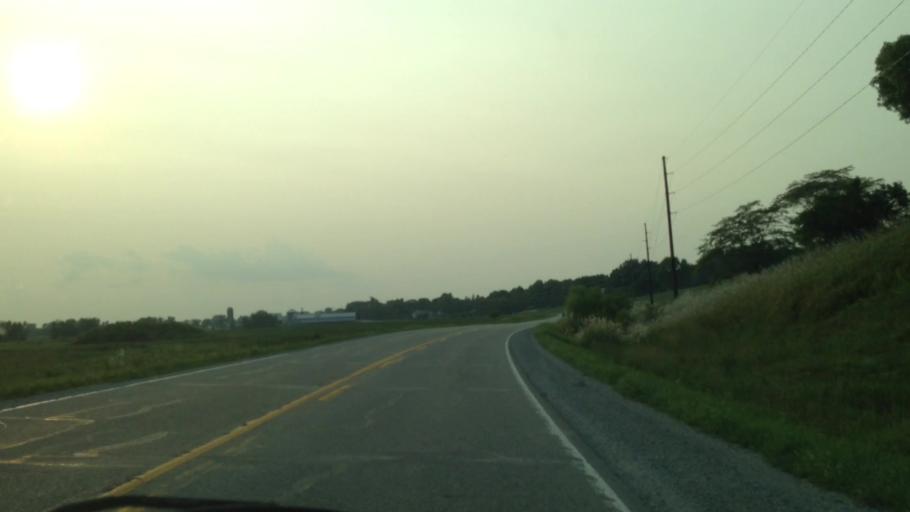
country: US
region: Iowa
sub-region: Benton County
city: Walford
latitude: 41.7989
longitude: -91.9303
